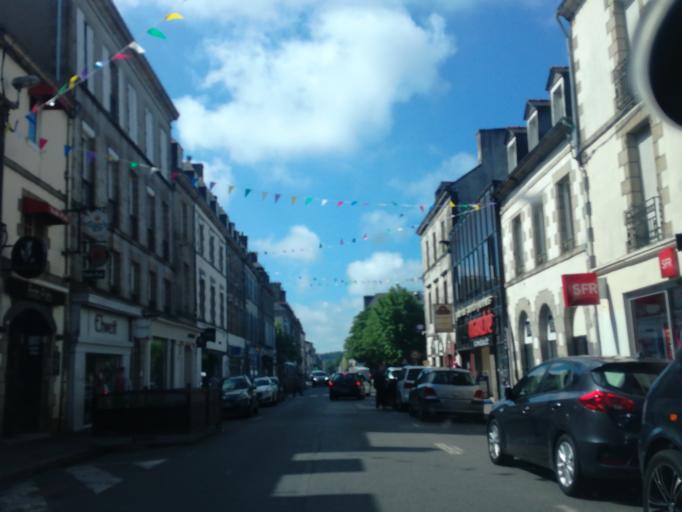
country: FR
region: Brittany
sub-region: Departement du Morbihan
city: Pontivy
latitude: 48.0660
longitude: -2.9656
